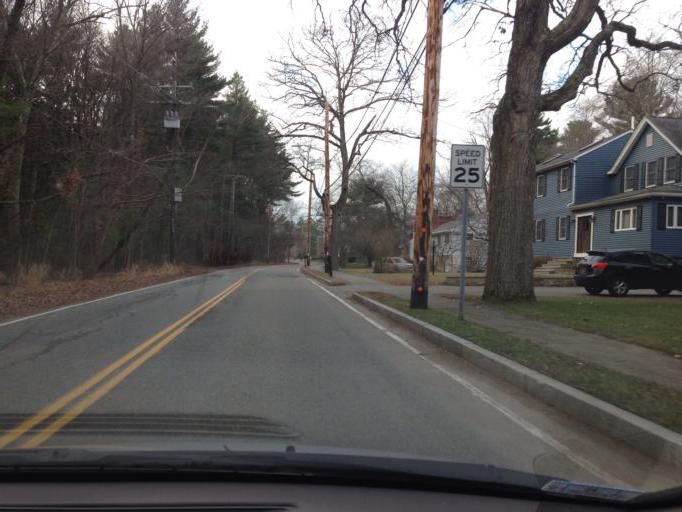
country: US
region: Massachusetts
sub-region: Middlesex County
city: Bedford
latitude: 42.4836
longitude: -71.2768
